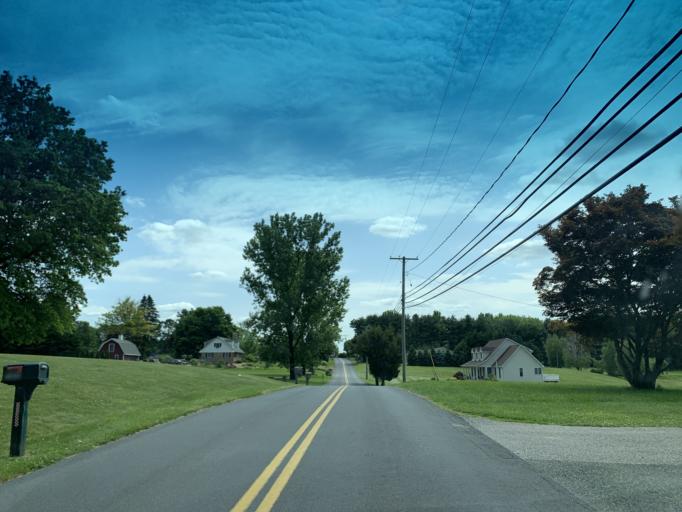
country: US
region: Maryland
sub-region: Harford County
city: Jarrettsville
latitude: 39.6305
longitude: -76.4628
